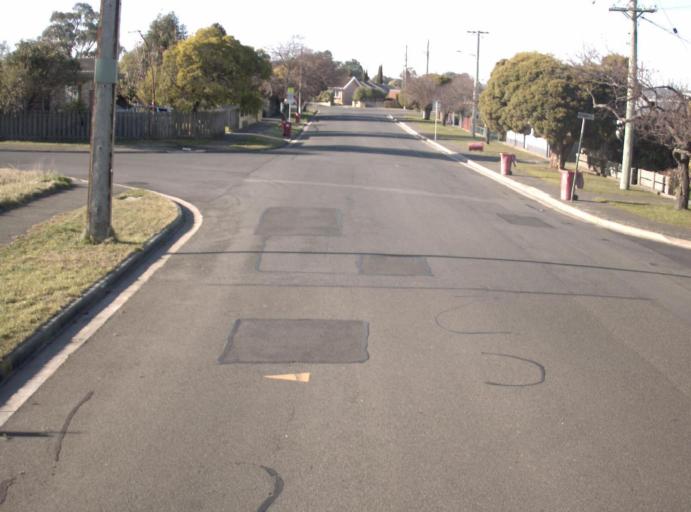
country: AU
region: Tasmania
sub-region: Launceston
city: Summerhill
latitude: -41.4690
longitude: 147.1215
